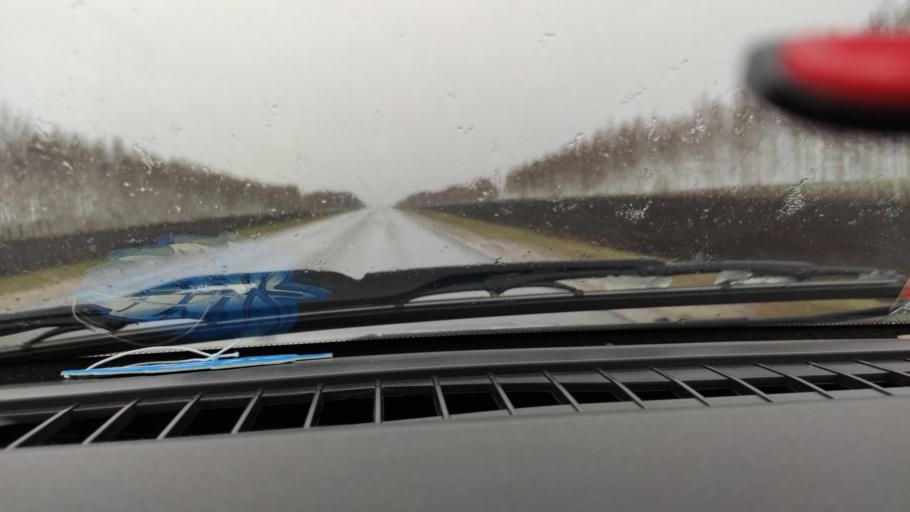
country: RU
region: Samara
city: Chelno-Vershiny
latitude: 54.6832
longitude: 51.0887
